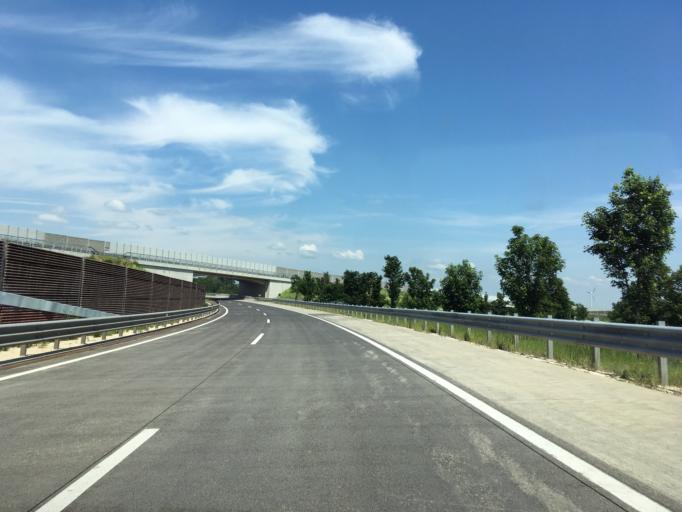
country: AT
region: Lower Austria
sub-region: Politischer Bezirk Mistelbach
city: Grossebersdorf
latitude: 48.3478
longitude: 16.4796
